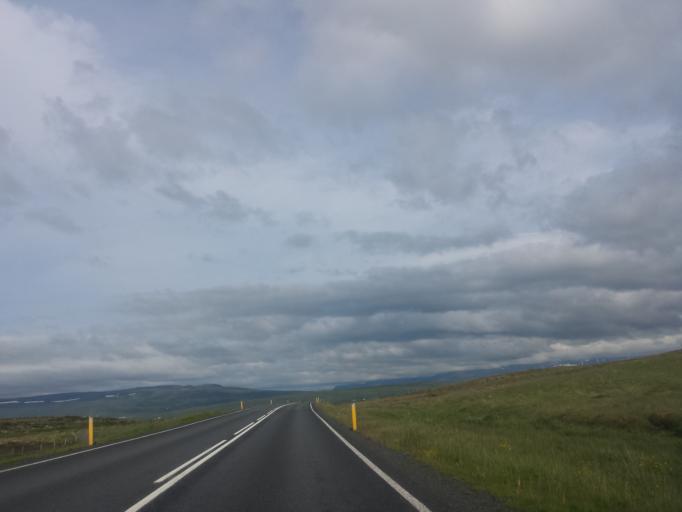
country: IS
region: West
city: Borgarnes
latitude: 65.3004
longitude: -20.9866
